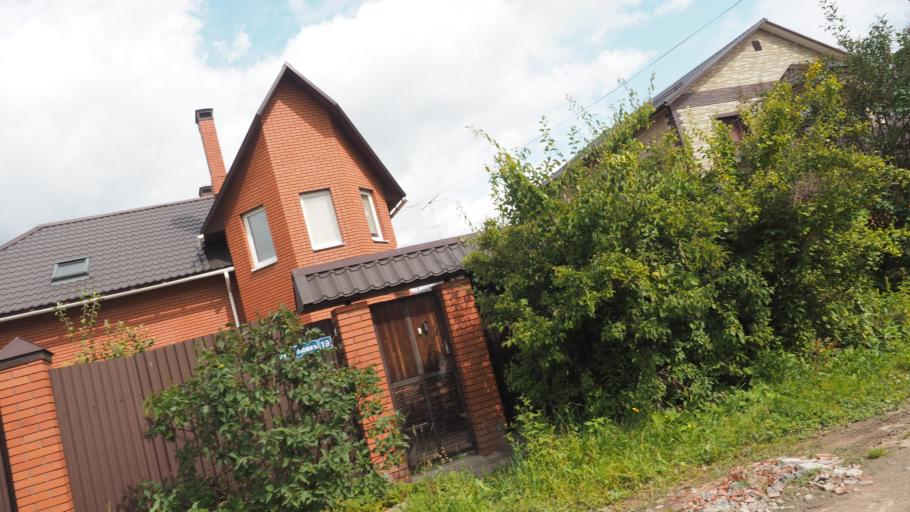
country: RU
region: Moskovskaya
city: Ramenskoye
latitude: 55.5775
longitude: 38.2598
